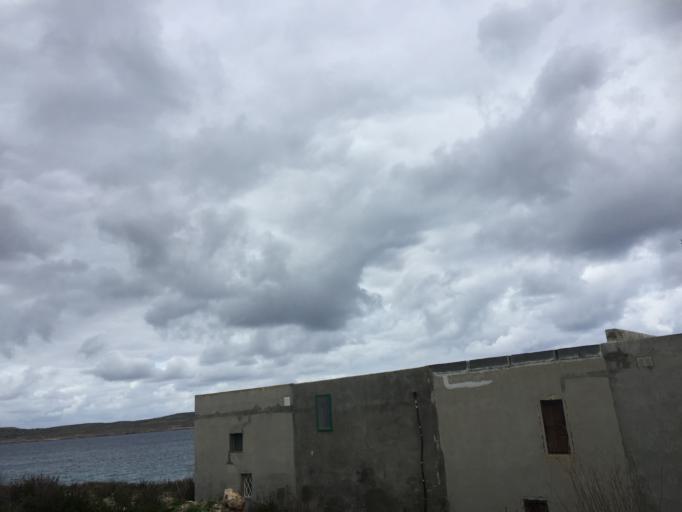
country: MT
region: Il-Mellieha
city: Mellieha
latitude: 35.9861
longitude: 14.3373
